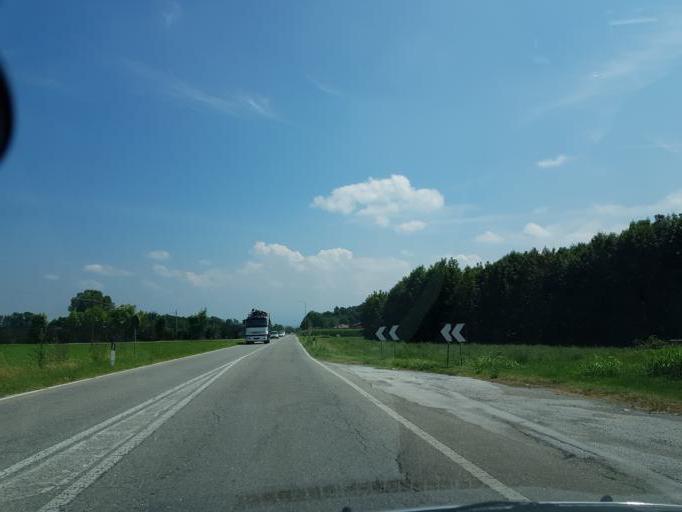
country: IT
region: Piedmont
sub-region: Provincia di Cuneo
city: Montemale di Cuneo
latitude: 44.4461
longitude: 7.4011
